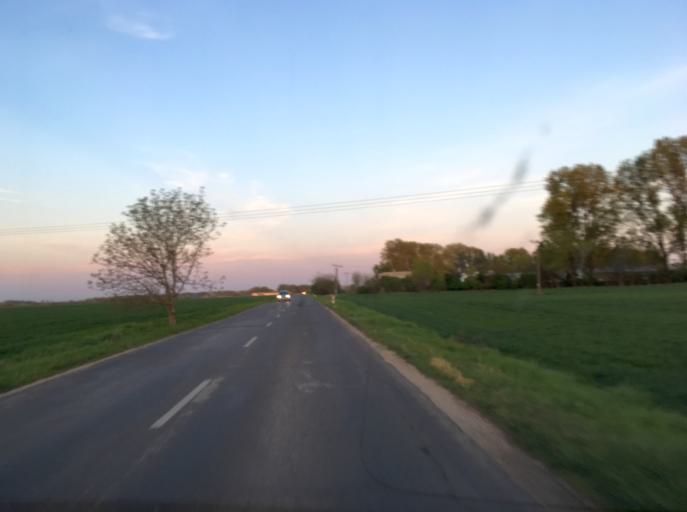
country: SK
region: Nitriansky
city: Kolarovo
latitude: 47.9254
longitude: 18.0187
